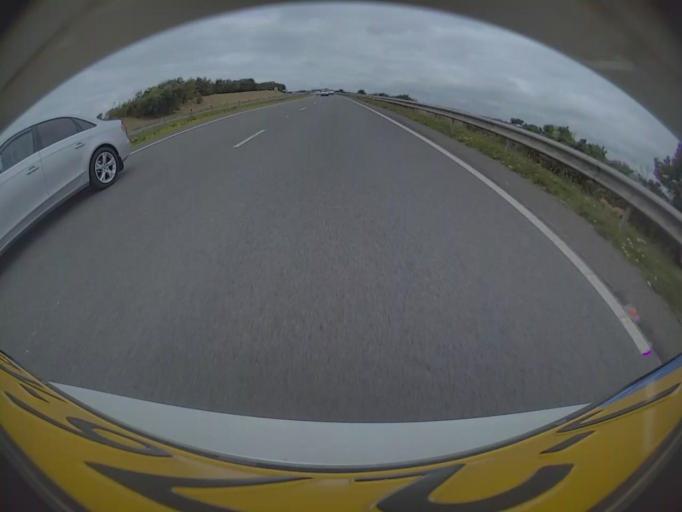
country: GB
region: Wales
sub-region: Anglesey
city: Llanfachraeth
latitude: 53.2700
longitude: -4.4893
